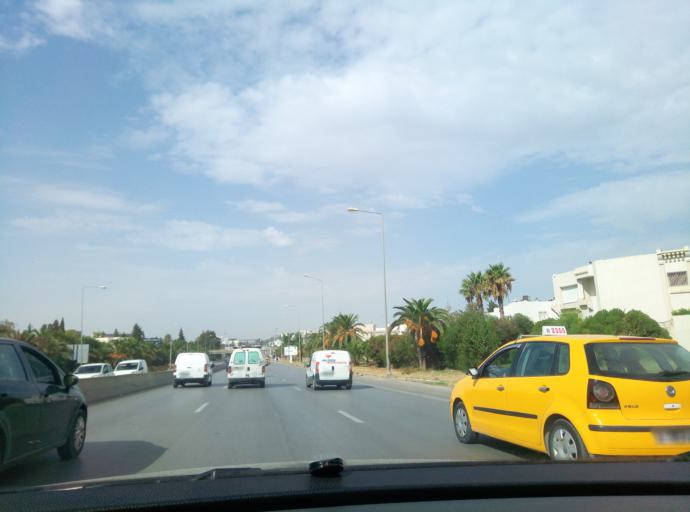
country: TN
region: Ariana
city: Ariana
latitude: 36.8436
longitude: 10.1752
